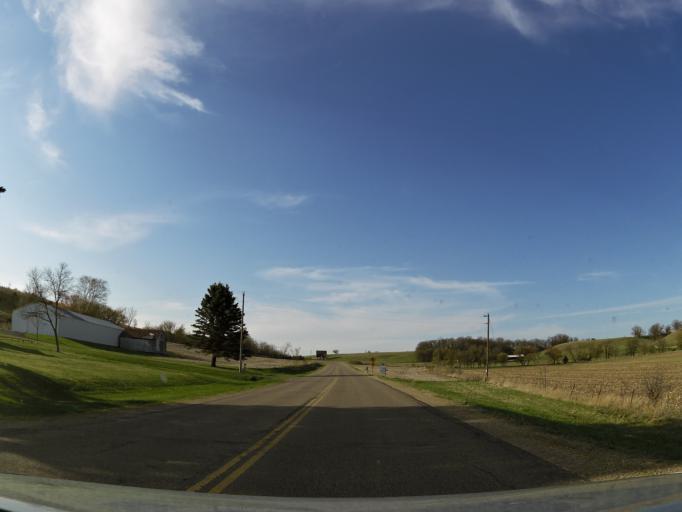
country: US
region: Wisconsin
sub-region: Pierce County
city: River Falls
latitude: 44.7800
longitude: -92.6398
